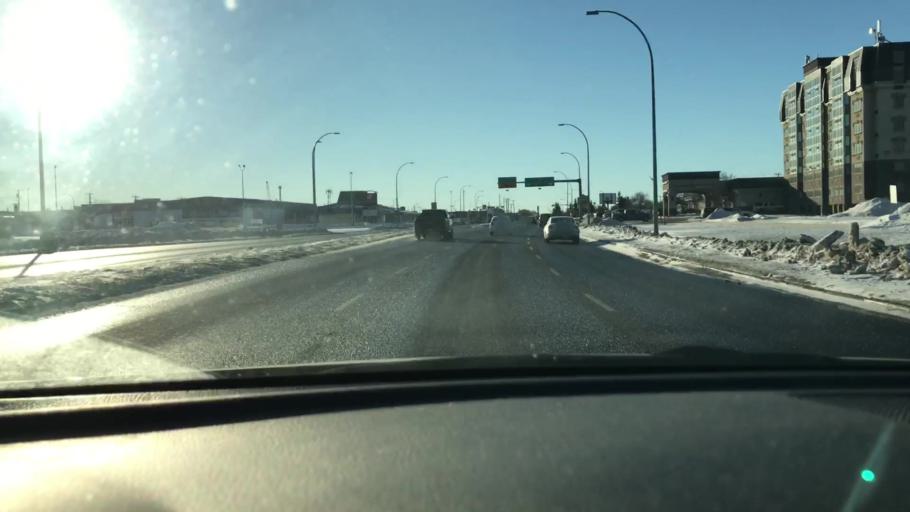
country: CA
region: Alberta
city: Edmonton
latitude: 53.5104
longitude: -113.4388
